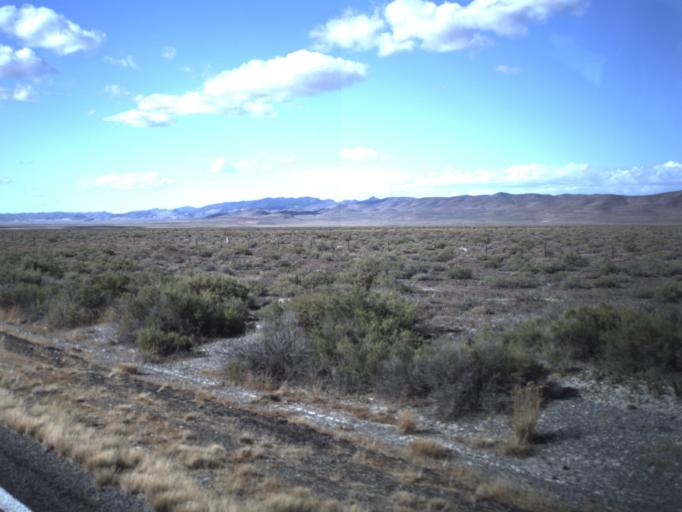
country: US
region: Utah
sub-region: Millard County
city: Delta
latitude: 39.1000
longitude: -112.7477
